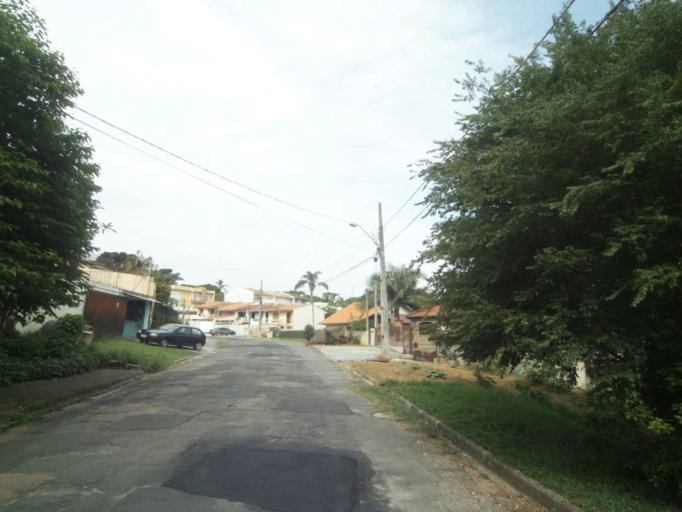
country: BR
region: Parana
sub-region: Curitiba
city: Curitiba
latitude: -25.4115
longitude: -49.2999
